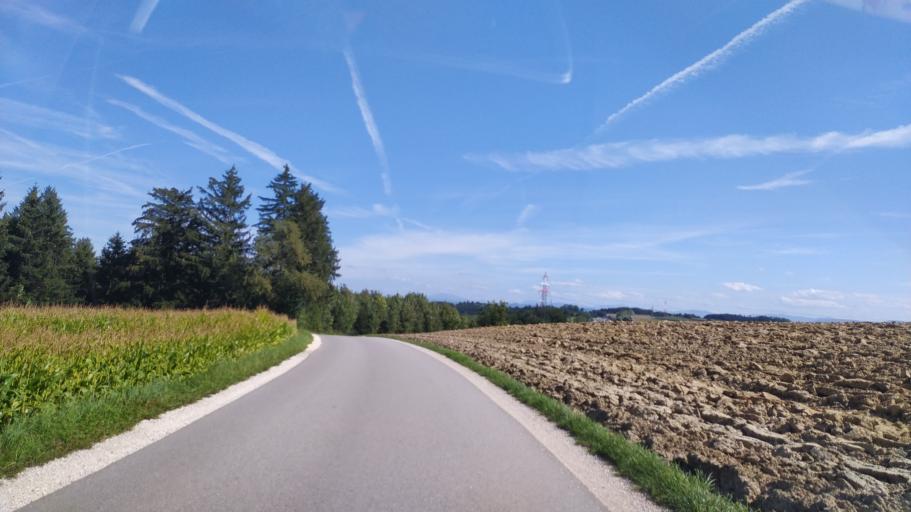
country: AT
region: Lower Austria
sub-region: Politischer Bezirk Amstetten
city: Strengberg
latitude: 48.1303
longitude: 14.6049
